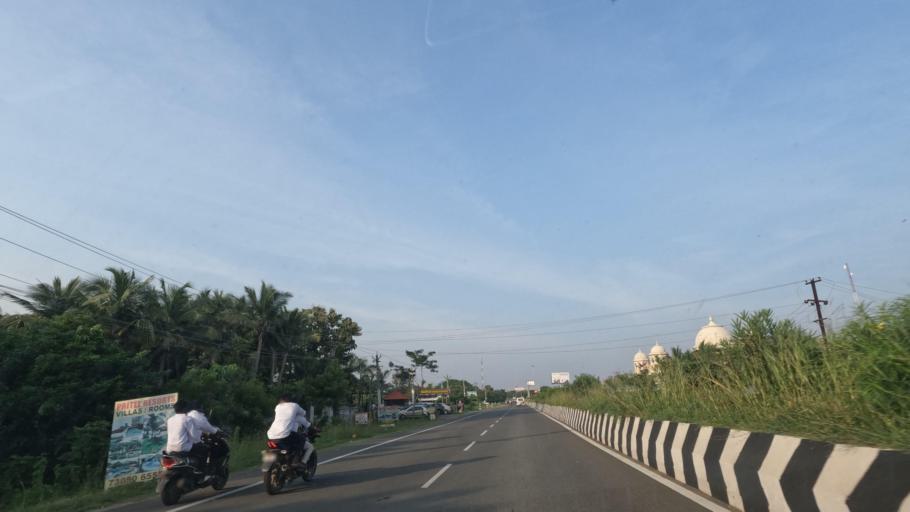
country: IN
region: Tamil Nadu
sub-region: Kancheepuram
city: Mamallapuram
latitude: 12.6454
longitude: 80.2014
